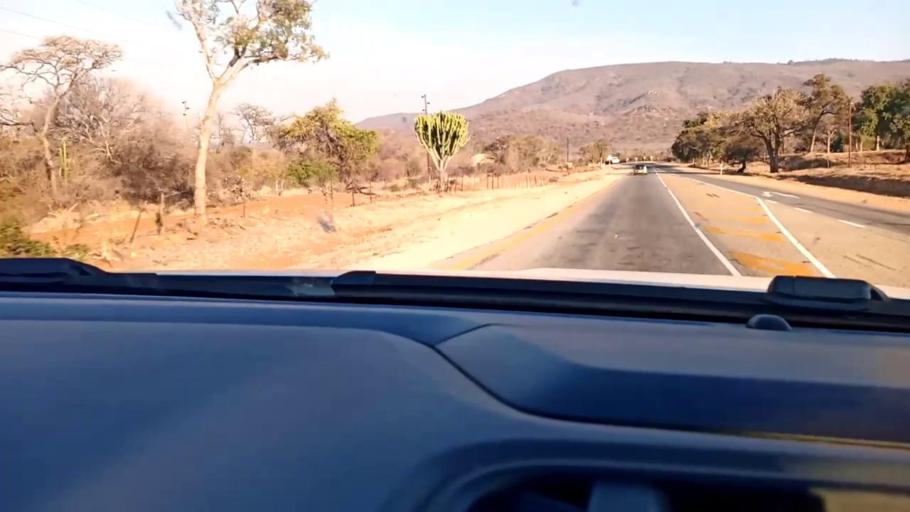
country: ZA
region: Limpopo
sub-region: Mopani District Municipality
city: Duiwelskloof
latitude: -23.6255
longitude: 30.1298
